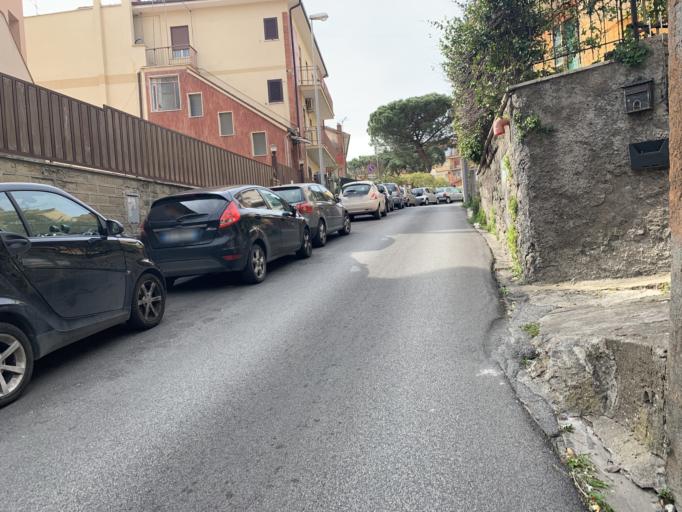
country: IT
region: Latium
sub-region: Citta metropolitana di Roma Capitale
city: Grottaferrata
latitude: 41.7681
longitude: 12.6662
